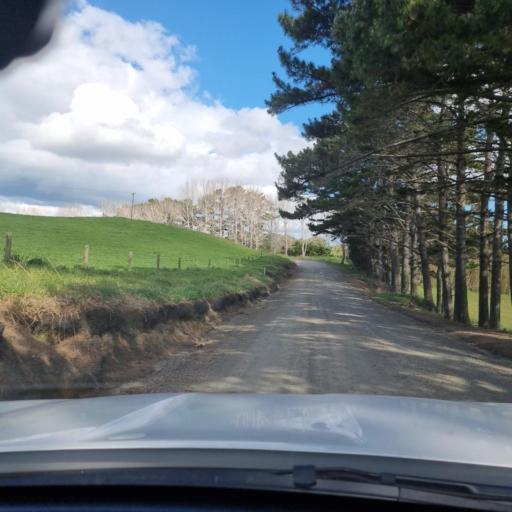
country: NZ
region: Auckland
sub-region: Auckland
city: Wellsford
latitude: -36.3266
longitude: 174.1424
